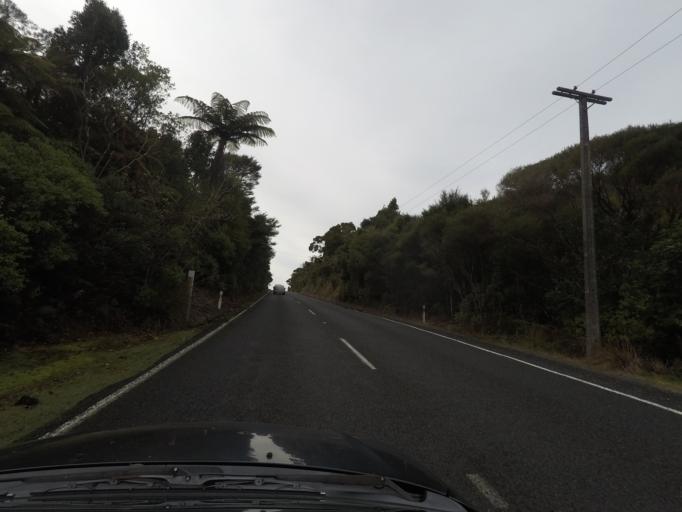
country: NZ
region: Auckland
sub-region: Auckland
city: Titirangi
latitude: -36.9476
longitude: 174.5239
